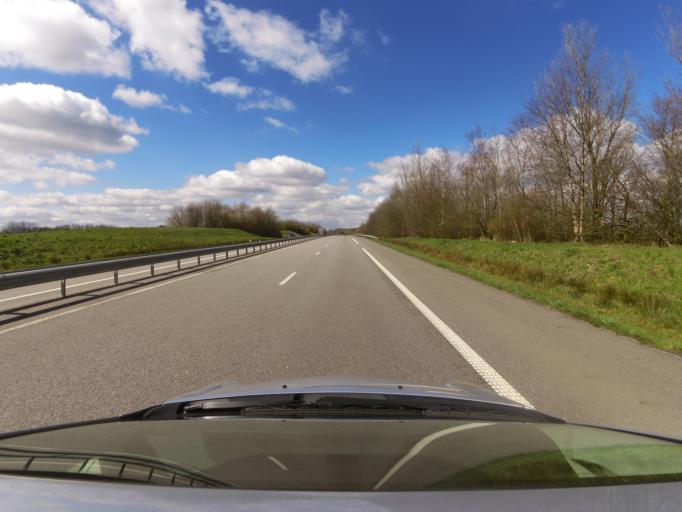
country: FR
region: Haute-Normandie
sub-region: Departement de la Seine-Maritime
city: Totes
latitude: 49.6404
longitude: 1.0239
